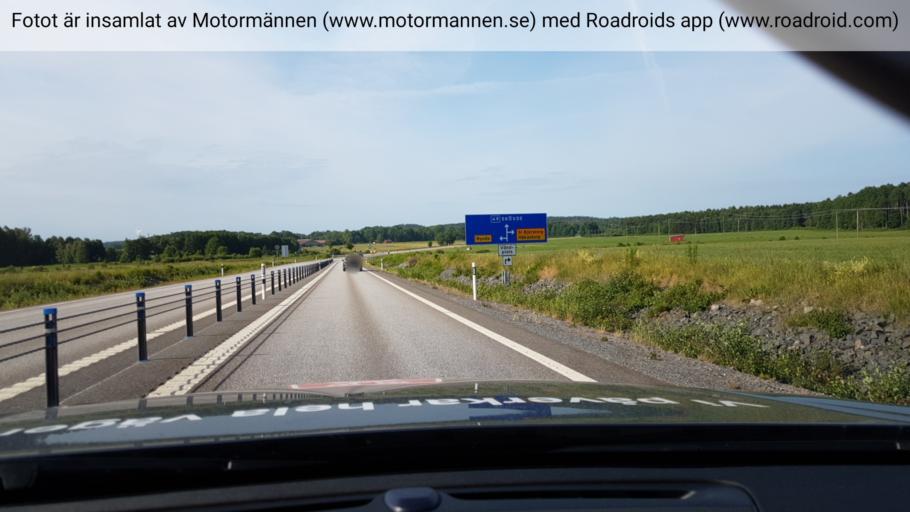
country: SE
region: OErebro
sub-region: Askersunds Kommun
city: Askersund
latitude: 58.7886
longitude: 14.8141
